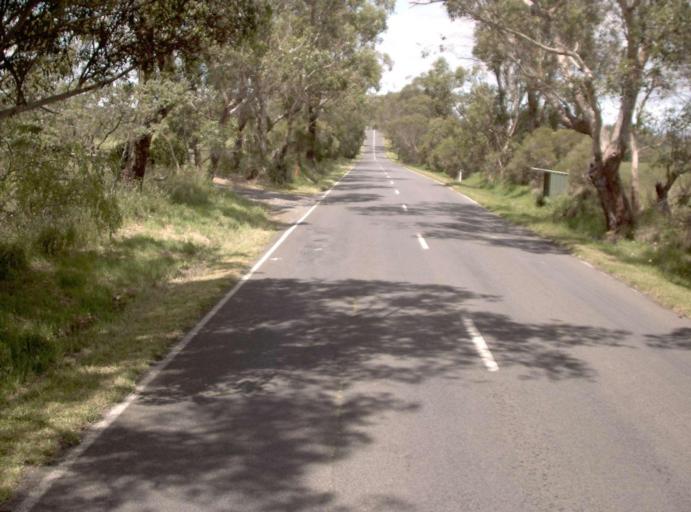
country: AU
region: Victoria
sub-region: Bass Coast
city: North Wonthaggi
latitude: -38.5939
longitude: 146.0205
